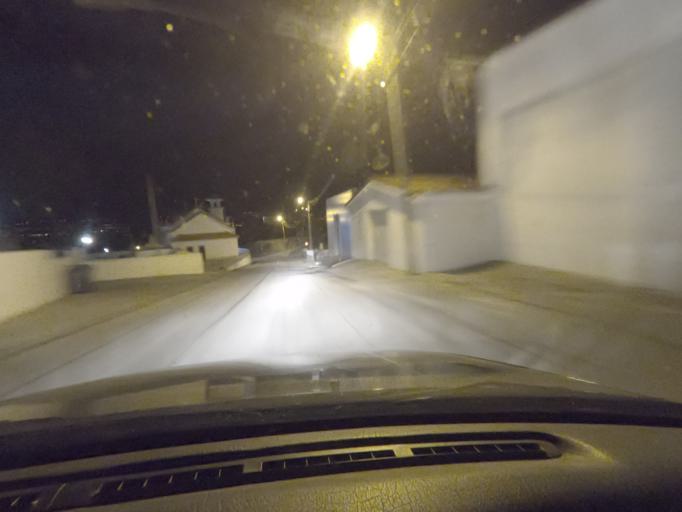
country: PT
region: Vila Real
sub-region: Santa Marta de Penaguiao
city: Santa Marta de Penaguiao
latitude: 41.2256
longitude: -7.8201
